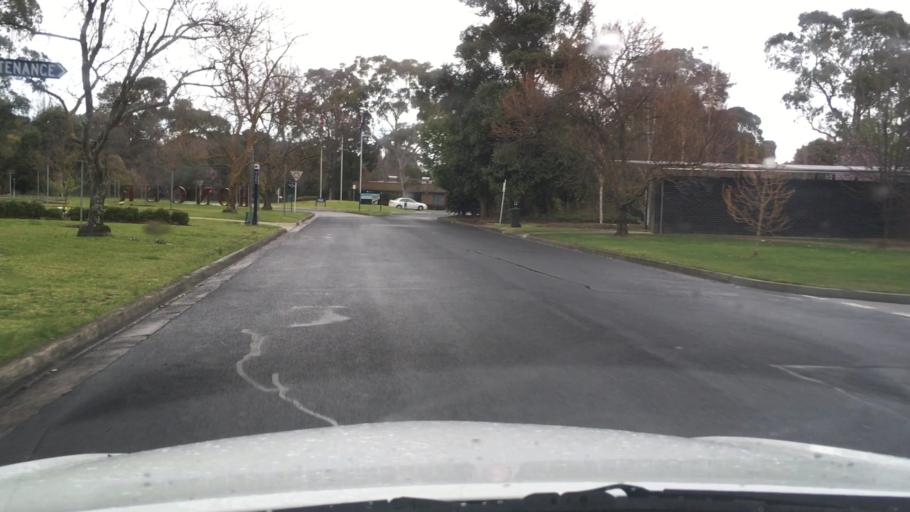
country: AU
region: Victoria
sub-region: Greater Dandenong
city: Noble Park North
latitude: -37.9447
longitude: 145.1770
